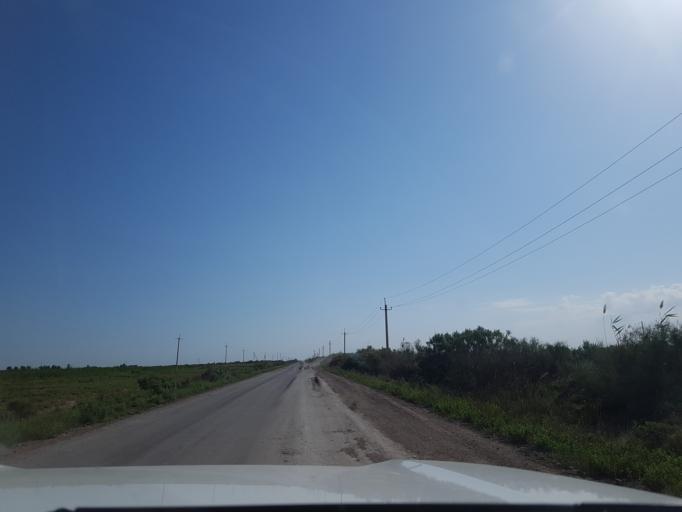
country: TM
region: Dasoguz
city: Koeneuergench
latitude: 42.0838
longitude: 58.8785
